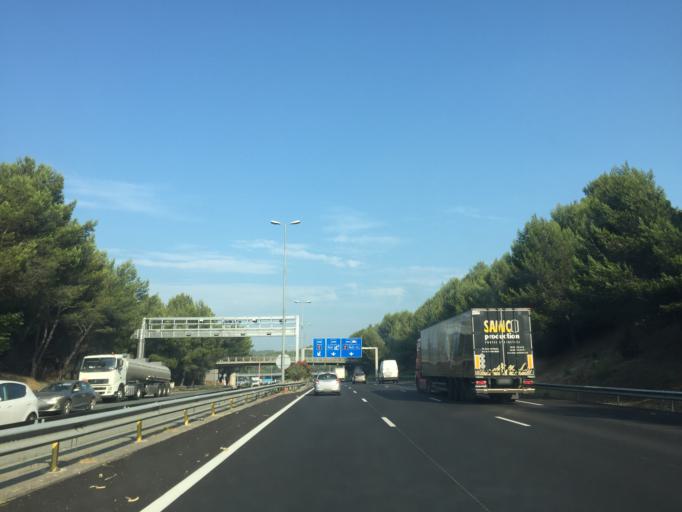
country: FR
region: Provence-Alpes-Cote d'Azur
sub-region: Departement des Alpes-Maritimes
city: Vallauris
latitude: 43.6035
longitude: 7.0722
